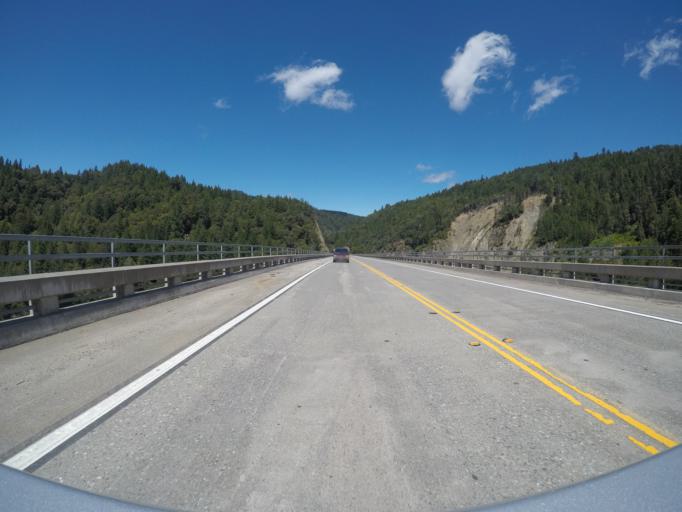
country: US
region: California
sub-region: Humboldt County
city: Redway
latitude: 39.9203
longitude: -123.7645
